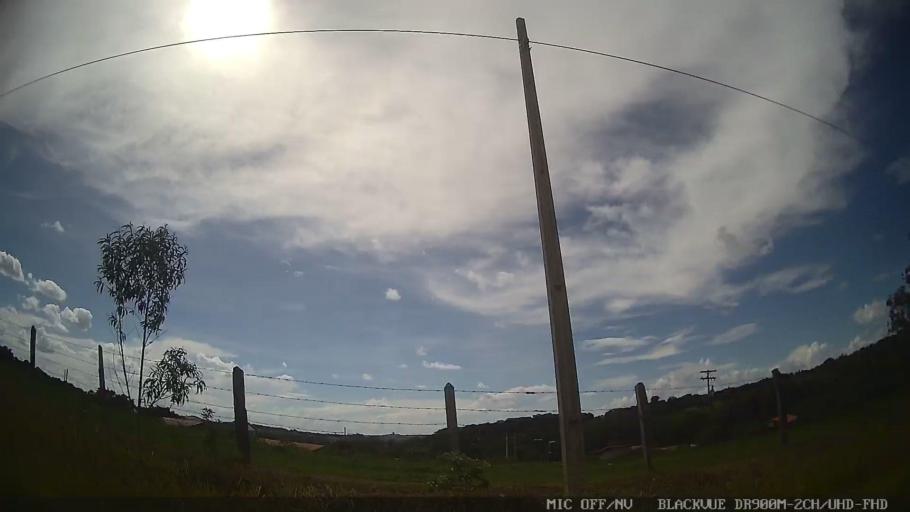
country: BR
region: Sao Paulo
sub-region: Conchas
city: Conchas
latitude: -22.9919
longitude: -47.9978
